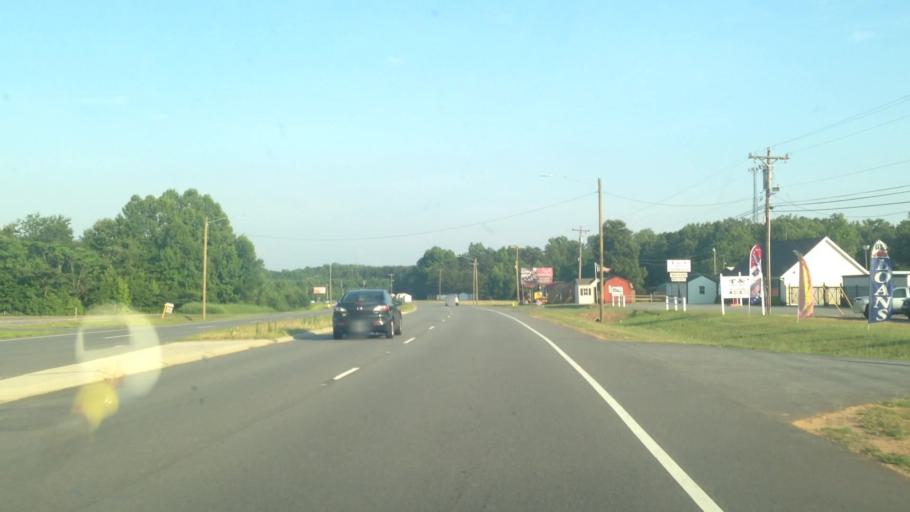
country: US
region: North Carolina
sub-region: Rockingham County
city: Reidsville
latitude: 36.3204
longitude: -79.6835
